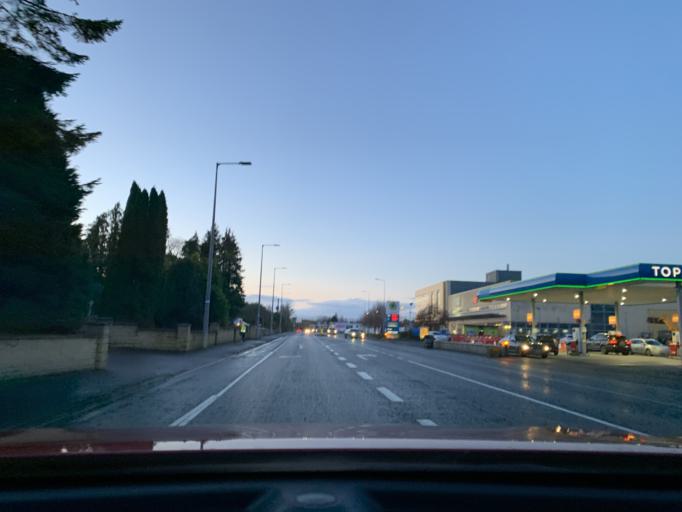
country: IE
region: Connaught
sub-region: County Leitrim
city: Carrick-on-Shannon
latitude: 53.9435
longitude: -8.0708
